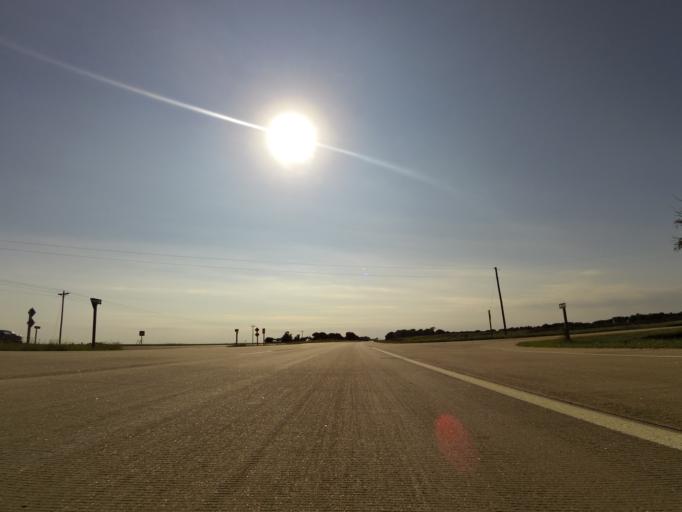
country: US
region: Kansas
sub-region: Sedgwick County
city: Colwich
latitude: 37.8251
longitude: -97.5366
